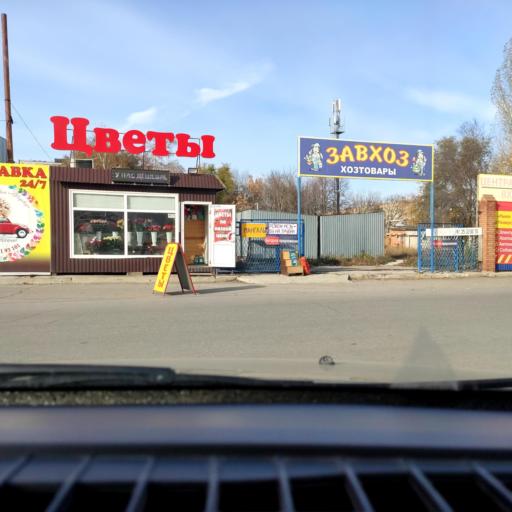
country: RU
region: Samara
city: Tol'yatti
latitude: 53.5195
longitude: 49.2712
